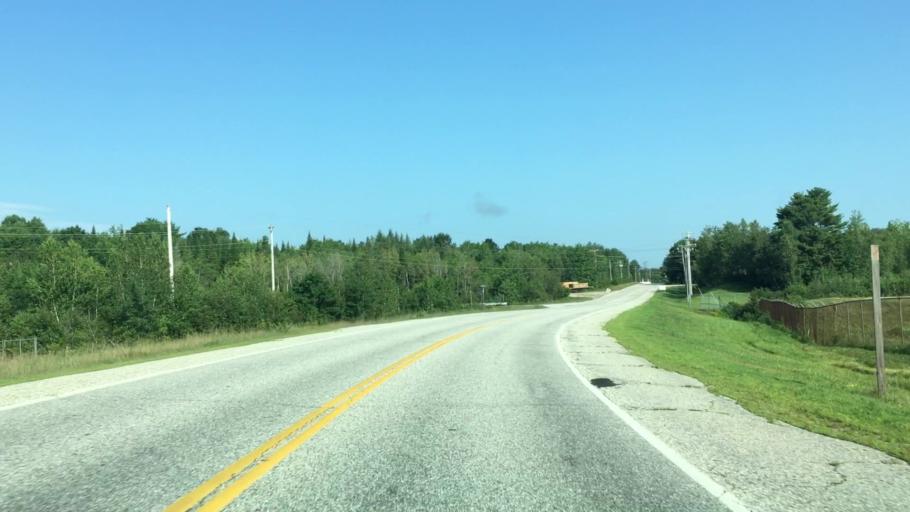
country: US
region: Maine
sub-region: Androscoggin County
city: Minot
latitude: 44.0409
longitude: -70.2905
